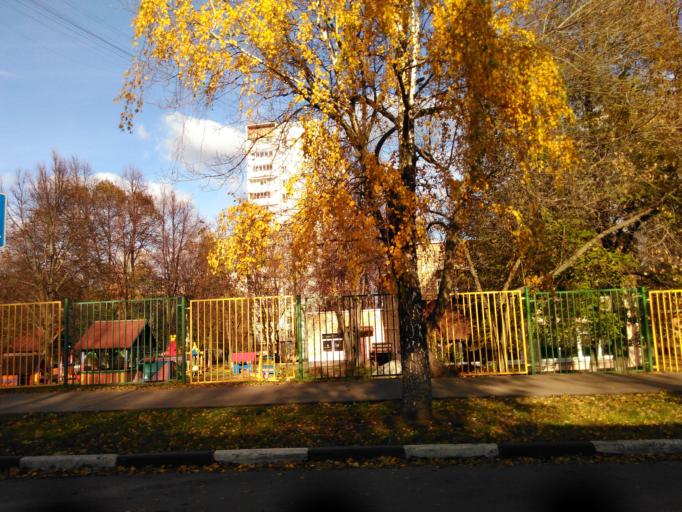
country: RU
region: Moscow
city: Zyuzino
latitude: 55.6510
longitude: 37.5727
